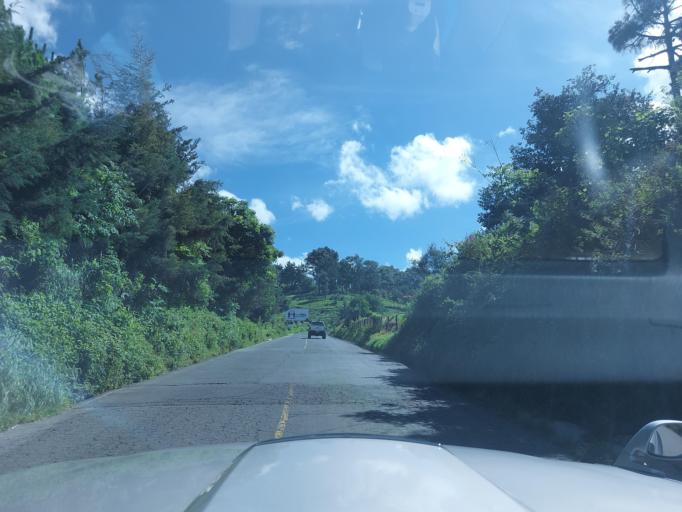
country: GT
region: Chimaltenango
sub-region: Municipio de San Juan Comalapa
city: Comalapa
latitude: 14.7181
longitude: -90.8890
